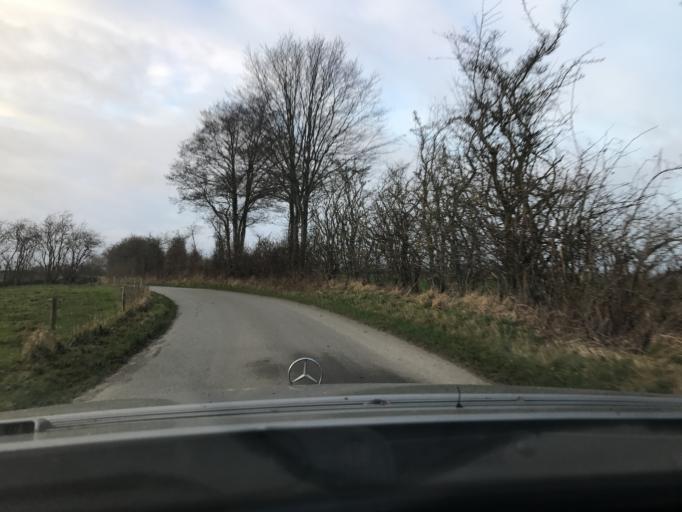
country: DK
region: South Denmark
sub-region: Sonderborg Kommune
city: Nordborg
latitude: 55.0523
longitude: 9.6867
